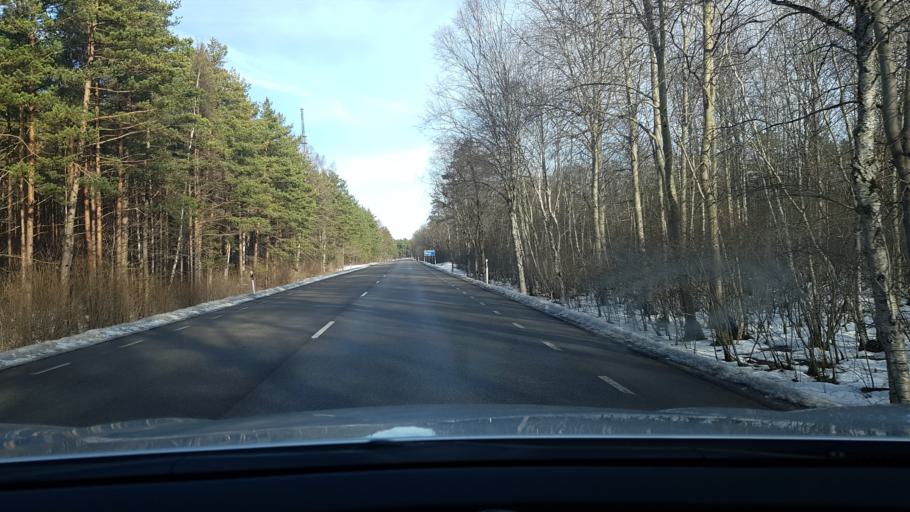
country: EE
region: Saare
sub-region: Orissaare vald
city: Orissaare
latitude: 58.5512
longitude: 23.0619
